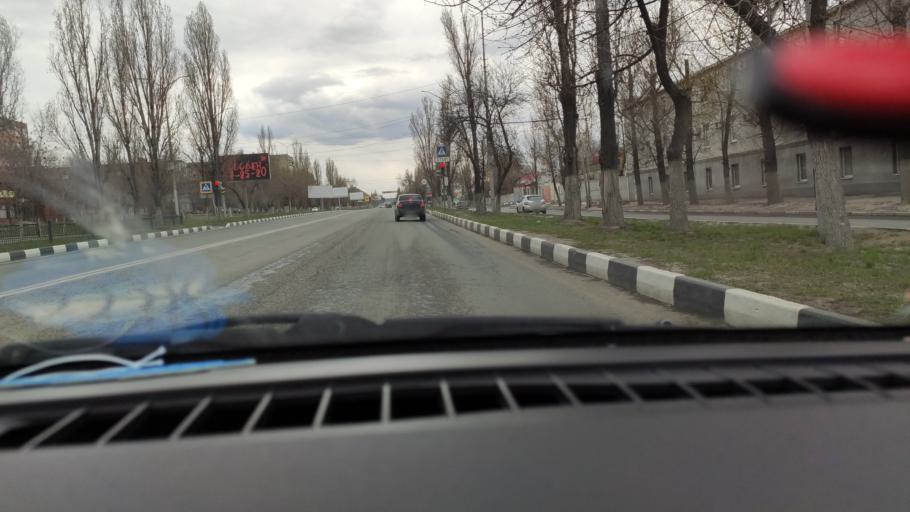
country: RU
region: Saratov
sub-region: Saratovskiy Rayon
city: Saratov
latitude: 51.6070
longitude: 45.9691
